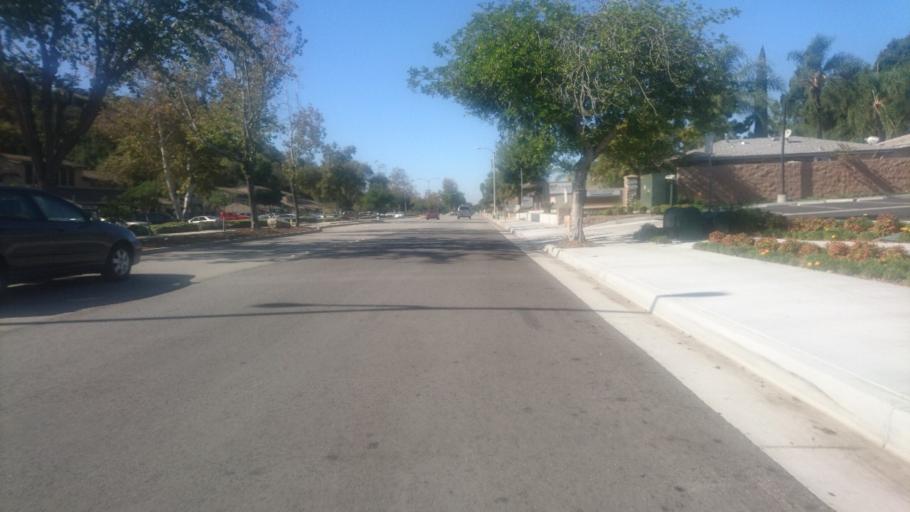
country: US
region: California
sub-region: Los Angeles County
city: Glendora
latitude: 34.1289
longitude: -117.8410
